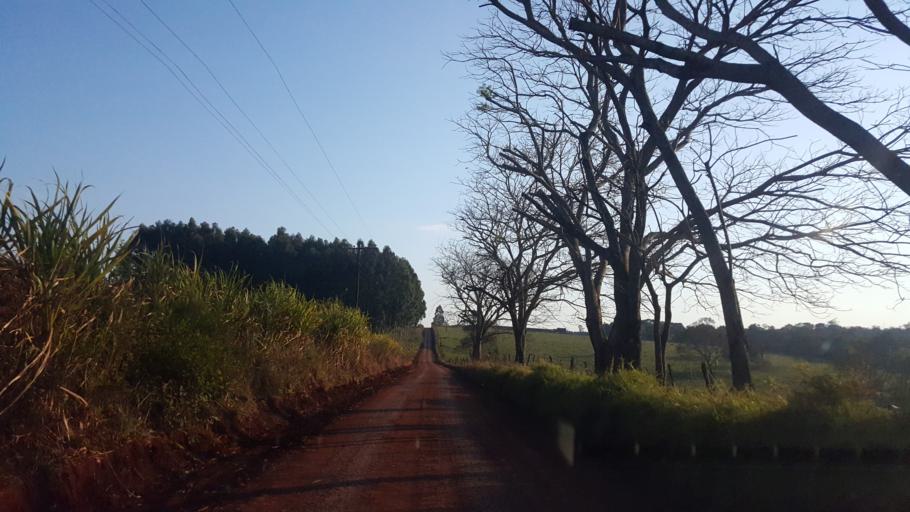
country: AR
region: Misiones
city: Capiovi
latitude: -26.9119
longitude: -55.0511
